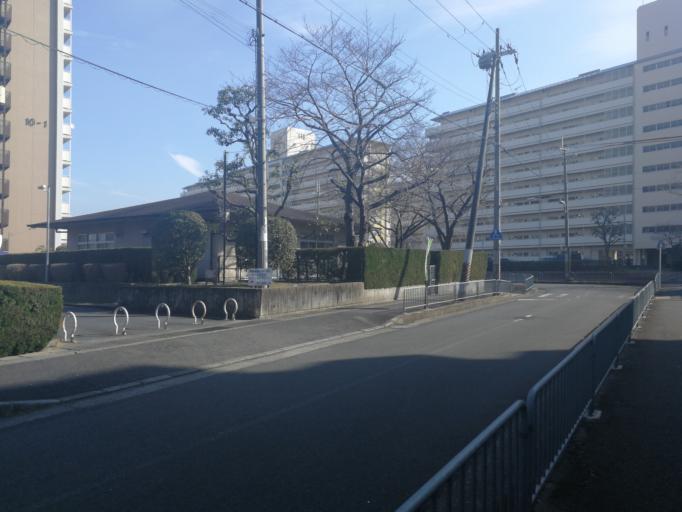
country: JP
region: Kyoto
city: Uji
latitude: 34.9189
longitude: 135.7804
